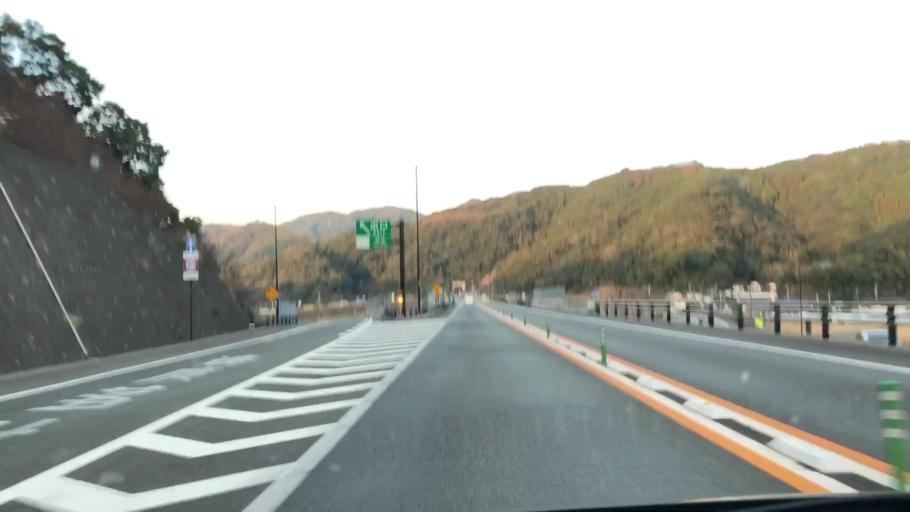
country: JP
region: Kumamoto
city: Minamata
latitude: 32.2965
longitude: 130.5084
